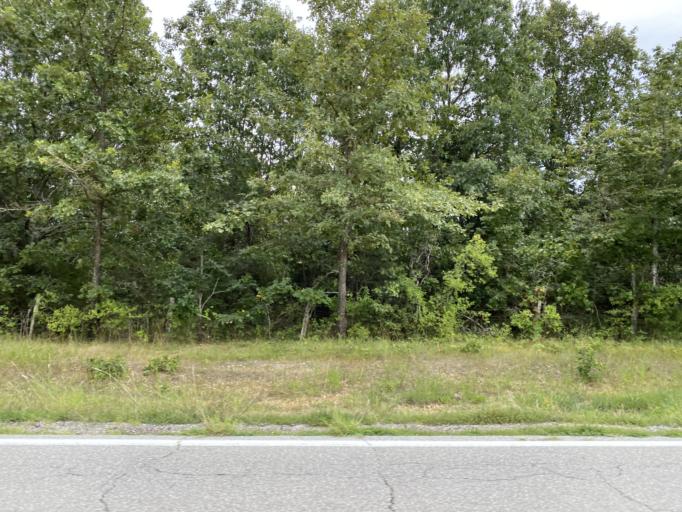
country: US
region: Arkansas
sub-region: Fulton County
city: Salem
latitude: 36.4284
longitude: -91.7045
